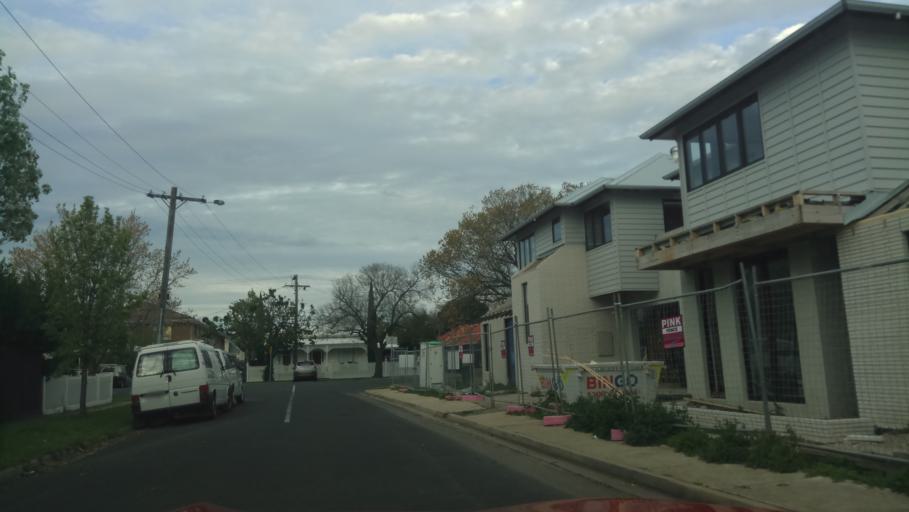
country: AU
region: Victoria
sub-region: Hobsons Bay
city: Williamstown
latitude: -37.8606
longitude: 144.8933
